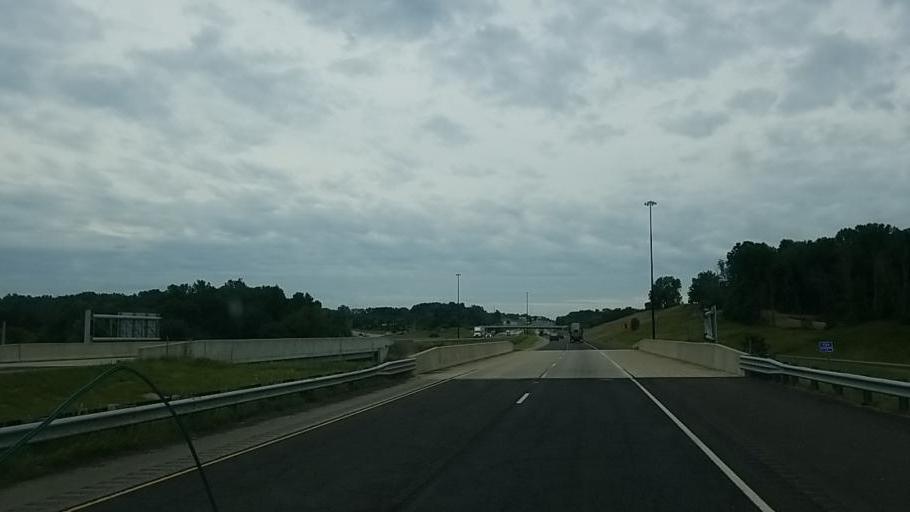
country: US
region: Indiana
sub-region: Steuben County
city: Angola
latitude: 41.7069
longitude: -85.0050
